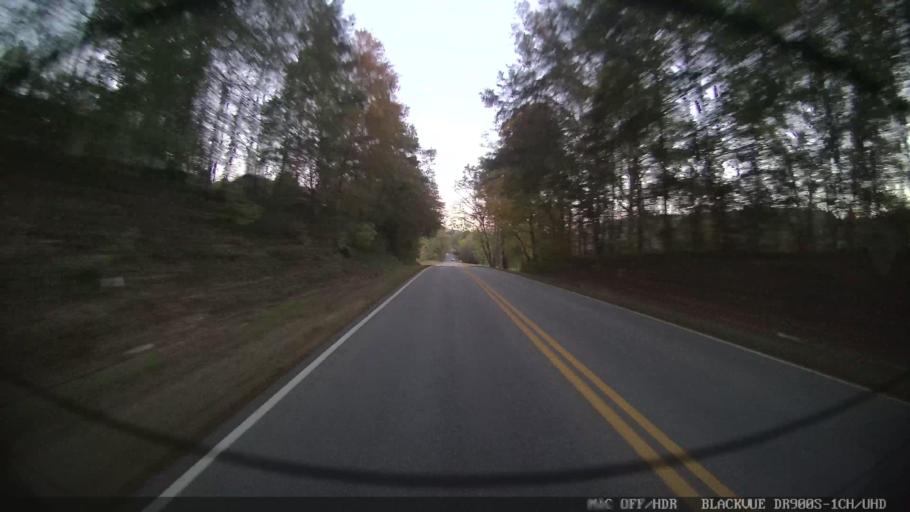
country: US
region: North Carolina
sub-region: Clay County
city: Hayesville
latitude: 34.9651
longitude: -83.8740
